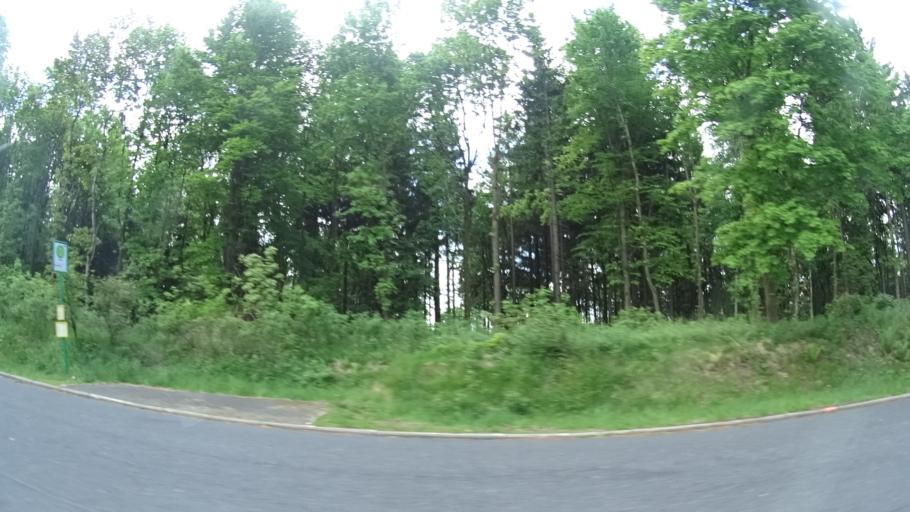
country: DE
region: Thuringia
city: Suhl
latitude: 50.6172
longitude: 10.7315
